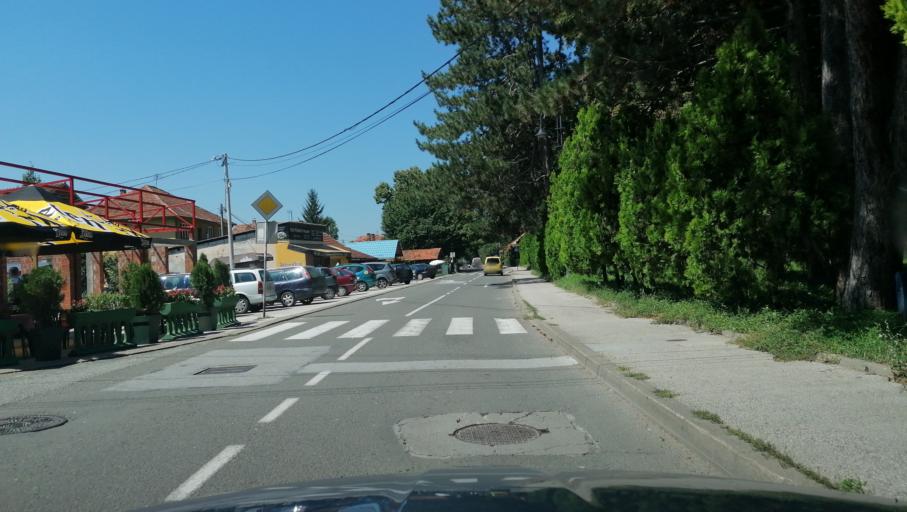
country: RS
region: Central Serbia
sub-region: Raski Okrug
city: Kraljevo
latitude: 43.6888
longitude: 20.6141
